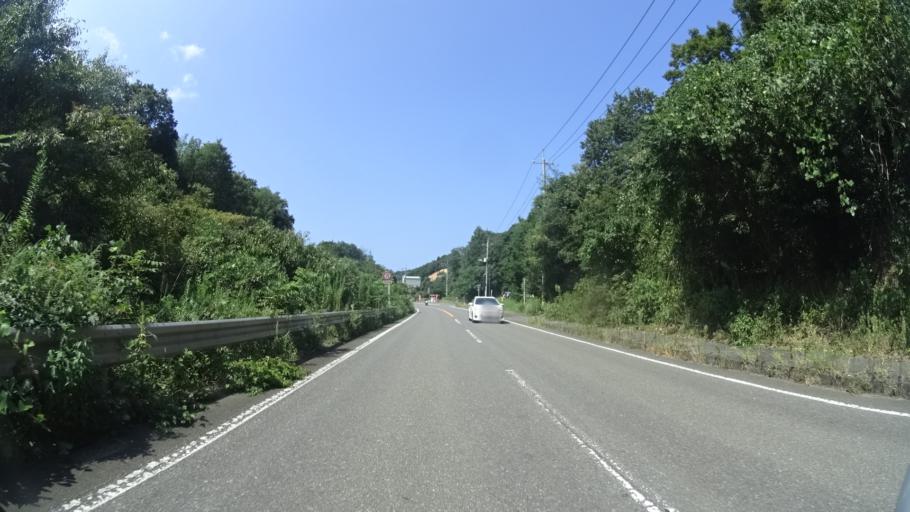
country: JP
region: Shimane
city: Masuda
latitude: 34.6258
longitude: 131.6242
